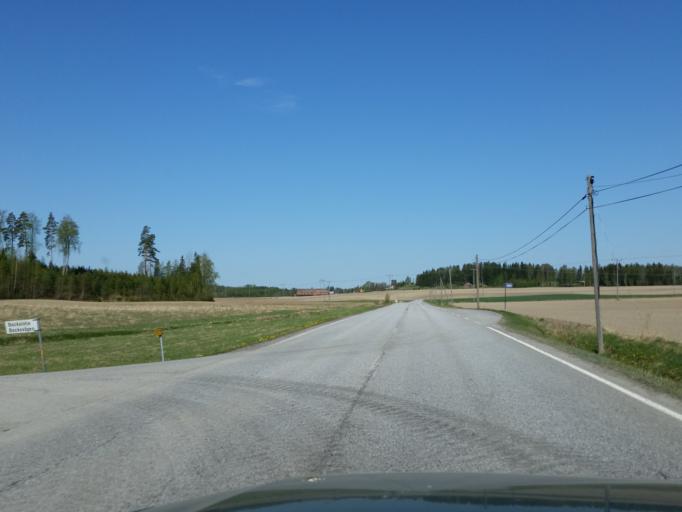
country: FI
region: Uusimaa
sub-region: Helsinki
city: Lohja
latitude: 60.1786
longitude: 24.0478
